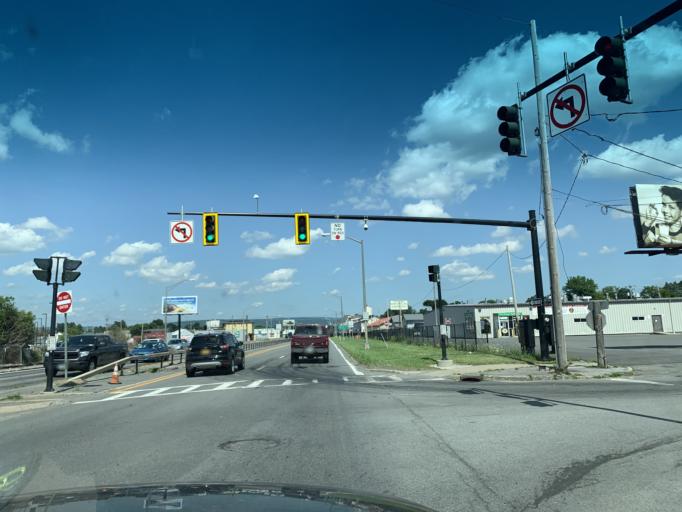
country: US
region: New York
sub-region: Oneida County
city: Utica
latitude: 43.0964
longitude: -75.2533
